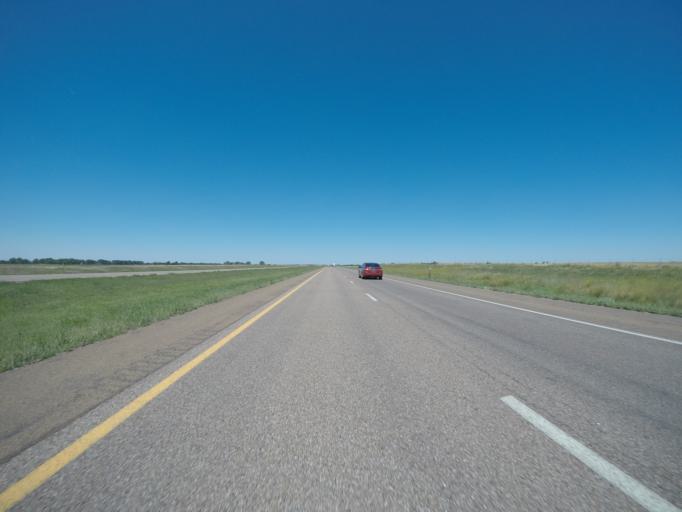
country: US
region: Kansas
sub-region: Ellis County
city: Ellis
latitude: 38.9638
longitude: -99.6388
